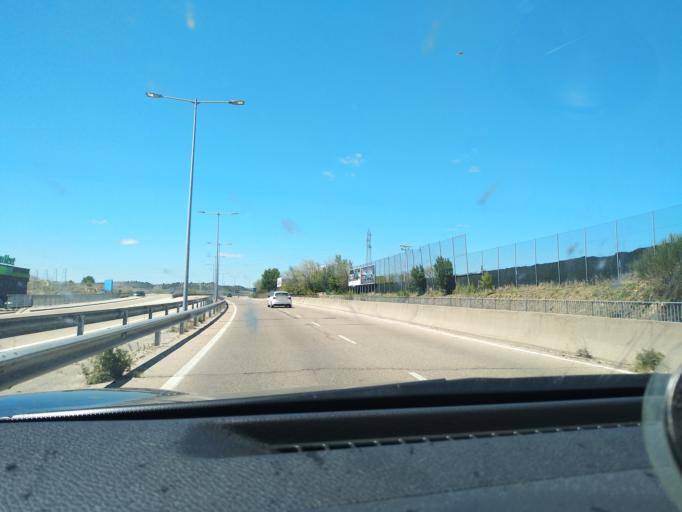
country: ES
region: Castille and Leon
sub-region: Provincia de Valladolid
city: Zaratan
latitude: 41.6433
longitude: -4.7622
